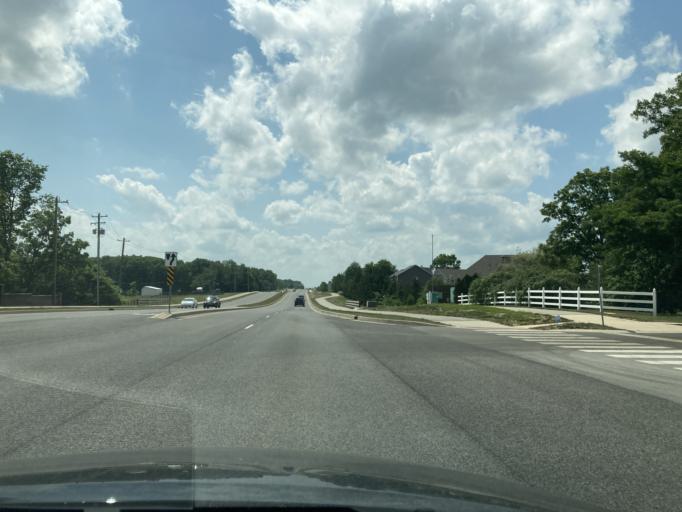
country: US
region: Indiana
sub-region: Hamilton County
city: Carmel
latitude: 39.9995
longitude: -86.1716
